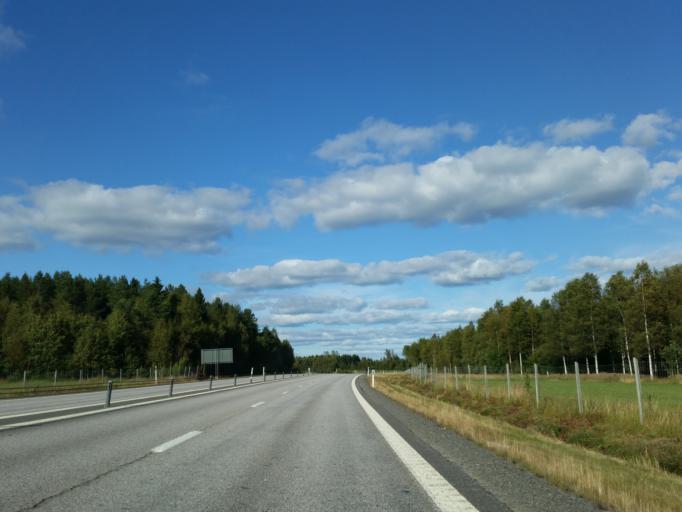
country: SE
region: Vaesterbotten
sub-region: Robertsfors Kommun
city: Robertsfors
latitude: 64.1412
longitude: 20.8956
